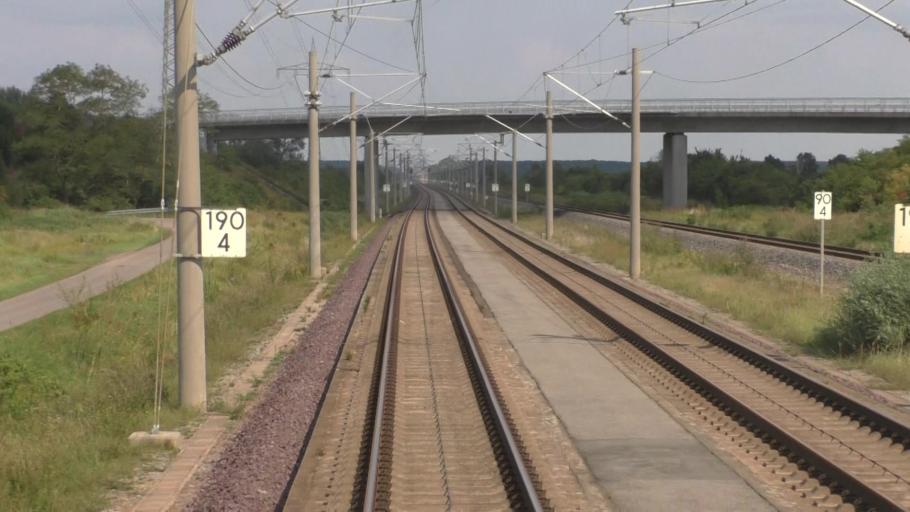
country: DE
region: Saxony-Anhalt
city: Schonhausen
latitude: 52.5904
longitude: 12.0676
